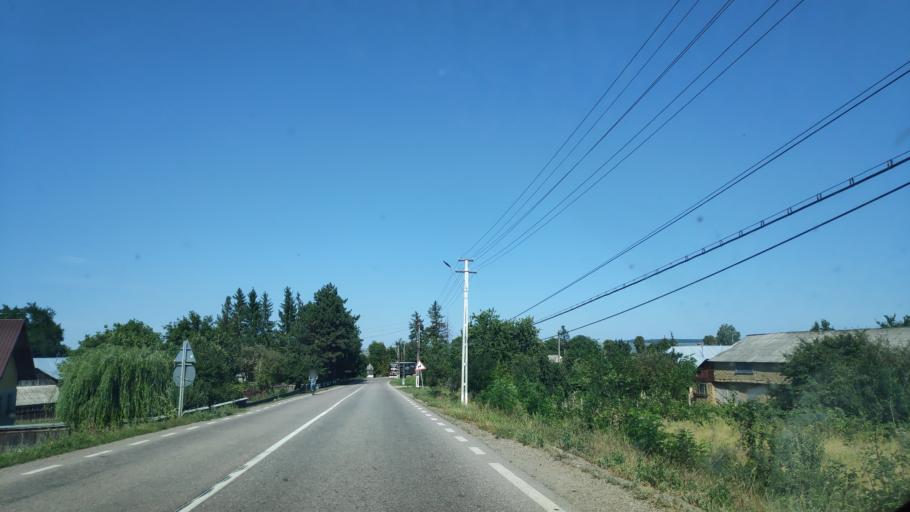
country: RO
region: Suceava
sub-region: Comuna Boroaia
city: Boroaia
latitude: 47.3515
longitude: 26.3357
